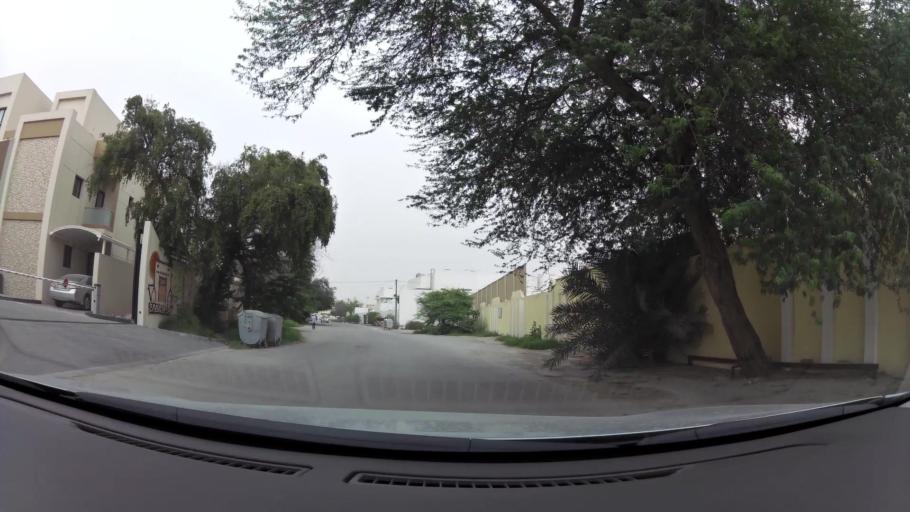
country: QA
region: Baladiyat ad Dawhah
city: Doha
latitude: 25.2580
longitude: 51.4953
